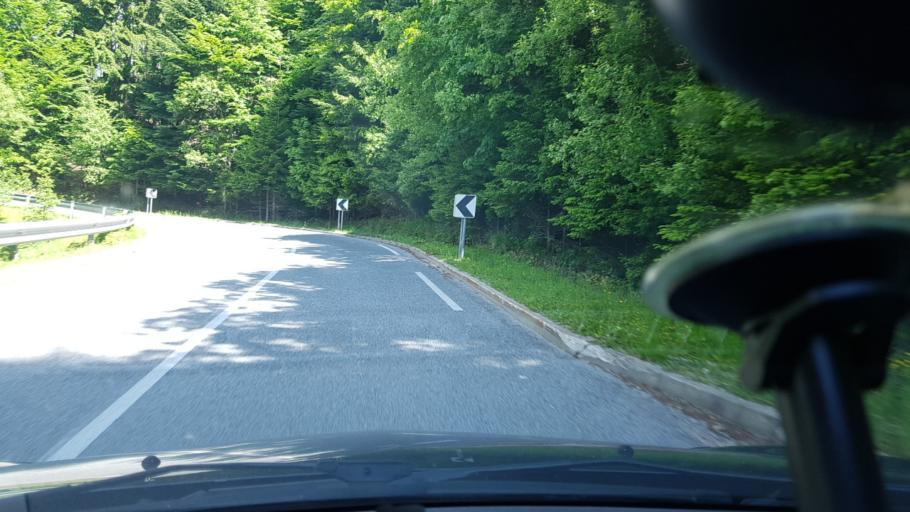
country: SI
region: Zrece
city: Zrece
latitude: 46.4361
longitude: 15.3686
